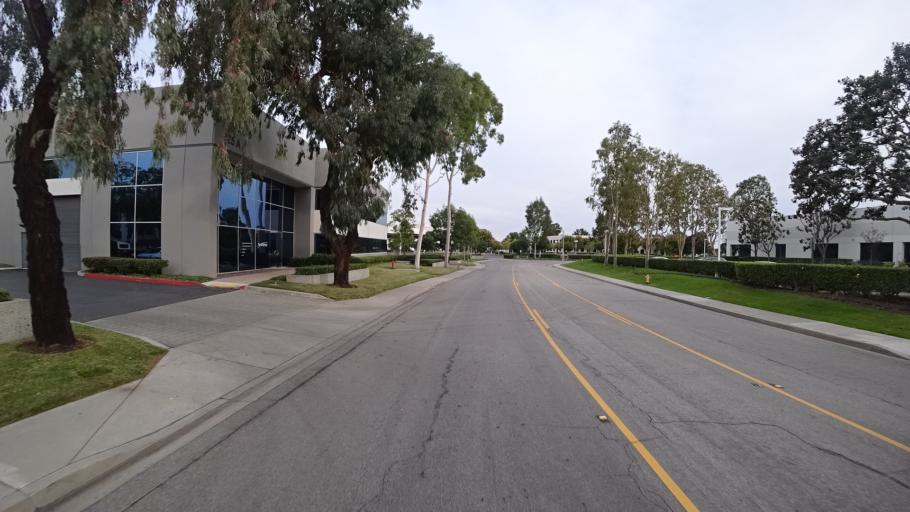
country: US
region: California
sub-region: Orange County
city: Laguna Woods
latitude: 33.5889
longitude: -117.7241
